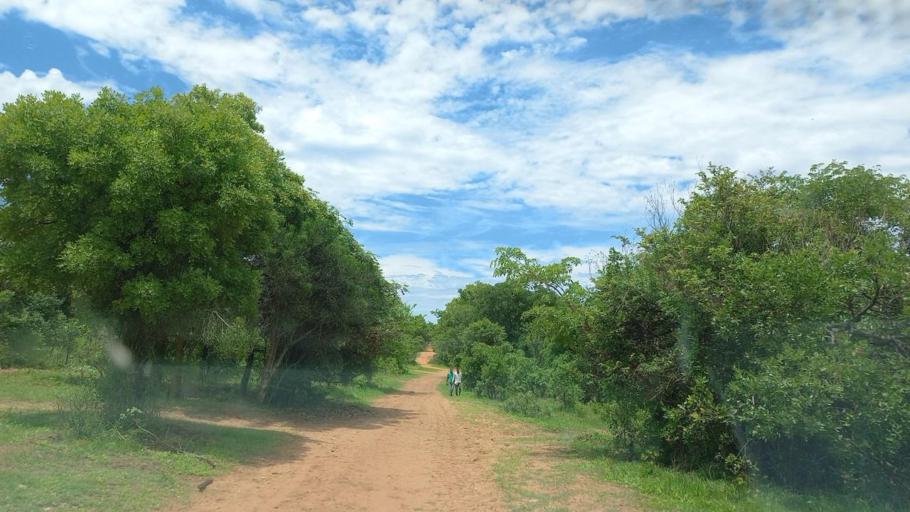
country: ZM
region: North-Western
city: Kabompo
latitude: -13.6108
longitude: 24.2437
